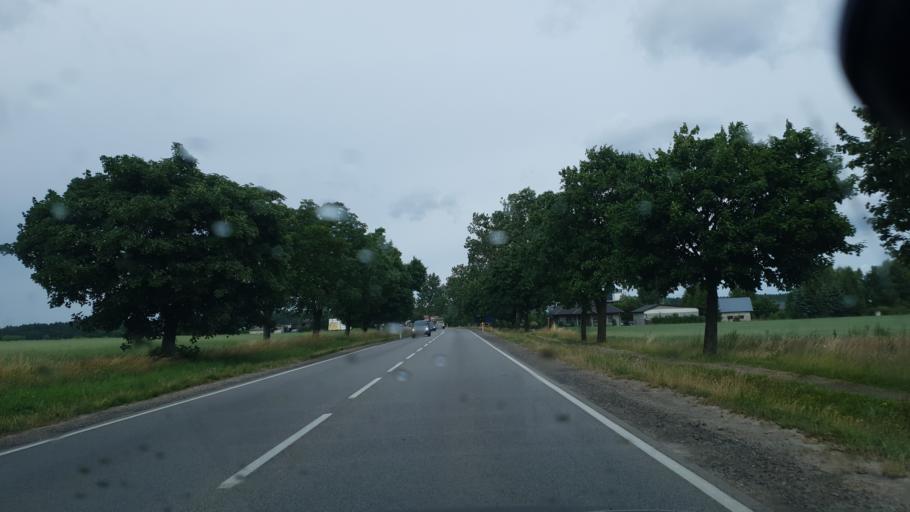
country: PL
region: Pomeranian Voivodeship
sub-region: Powiat kartuski
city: Banino
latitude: 54.4239
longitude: 18.3842
